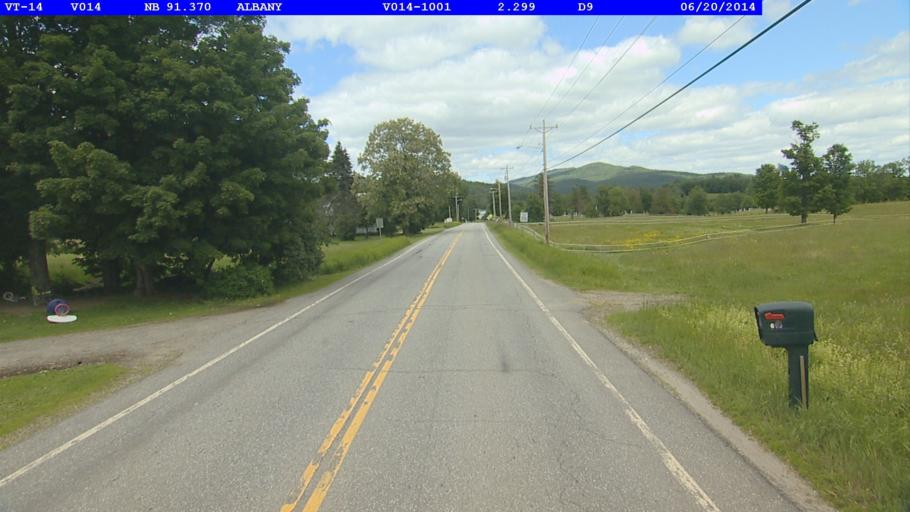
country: US
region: Vermont
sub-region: Caledonia County
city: Hardwick
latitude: 44.7341
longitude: -72.3788
